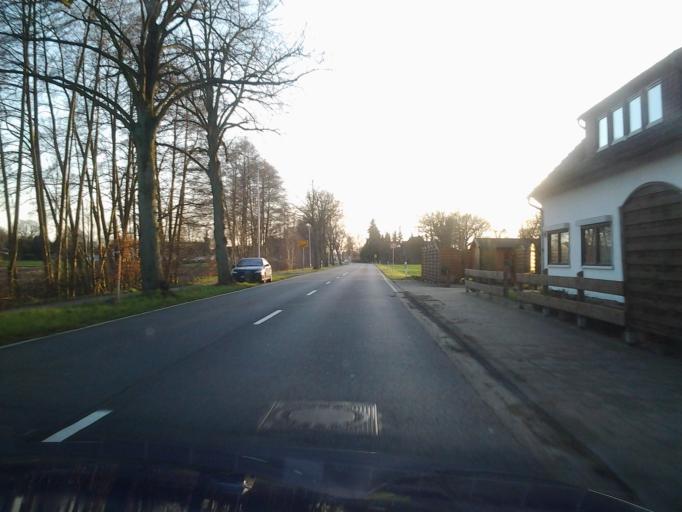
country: DE
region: Lower Saxony
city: Lilienthal
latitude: 53.1673
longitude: 8.9276
